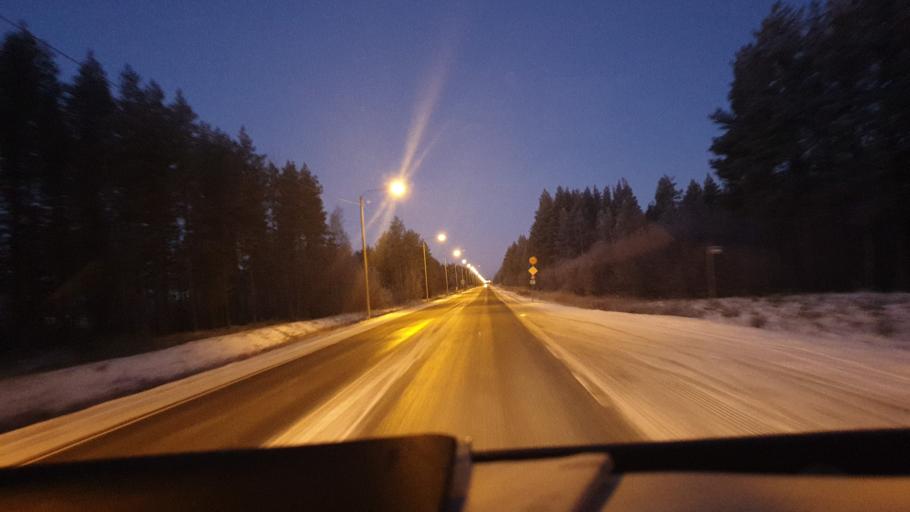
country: FI
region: Northern Ostrobothnia
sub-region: Raahe
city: Raahe
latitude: 64.6913
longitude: 24.6431
